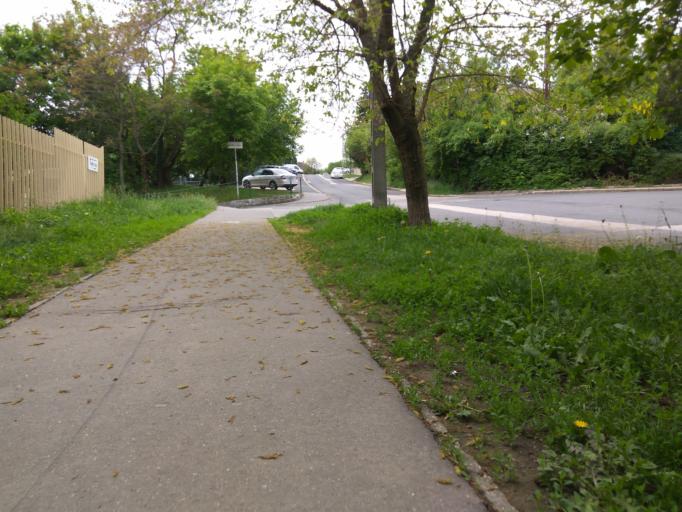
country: HU
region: Budapest
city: Budapest XII. keruelet
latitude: 47.4888
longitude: 19.0015
